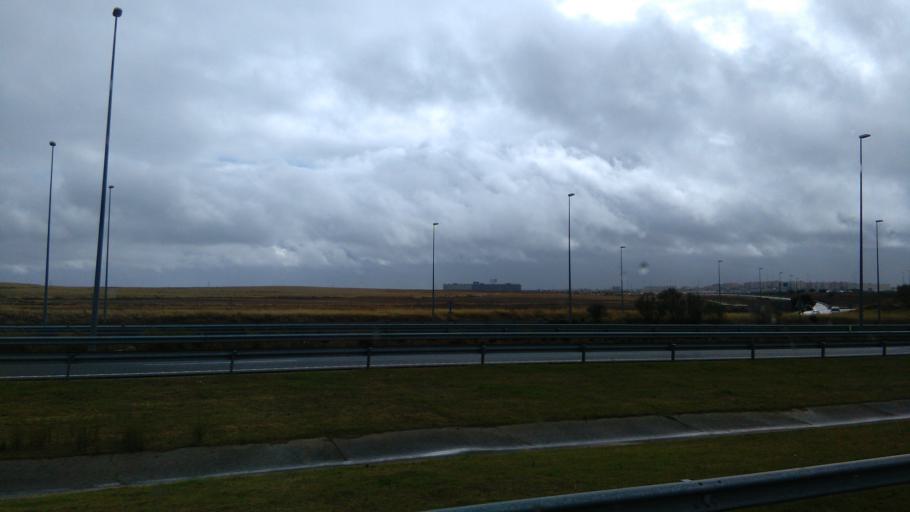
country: ES
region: Madrid
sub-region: Provincia de Madrid
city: Alcorcon
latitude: 40.3216
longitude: -3.8193
